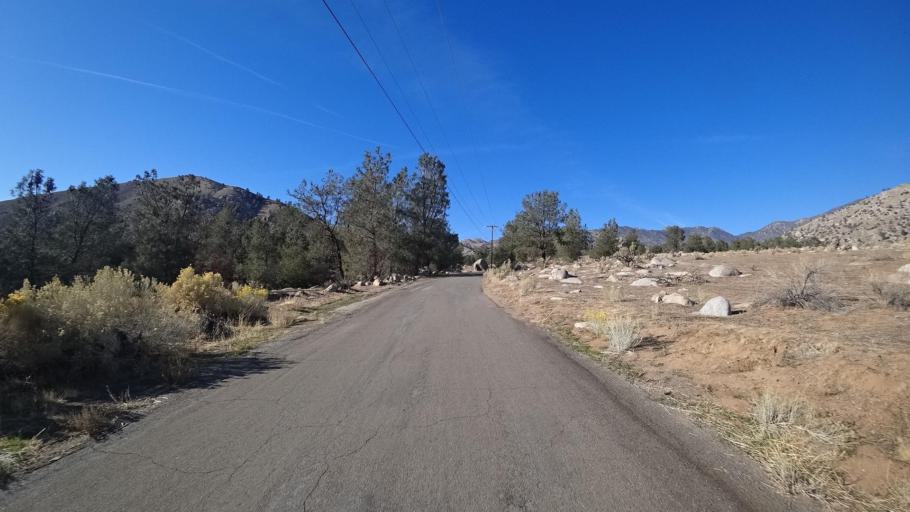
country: US
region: California
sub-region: Kern County
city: Weldon
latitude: 35.6979
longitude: -118.2968
